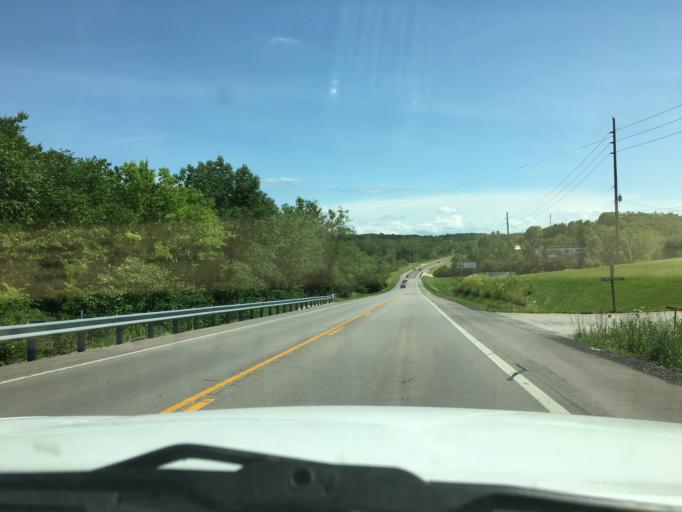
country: US
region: Missouri
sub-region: Franklin County
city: Union
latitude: 38.5017
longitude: -91.0043
